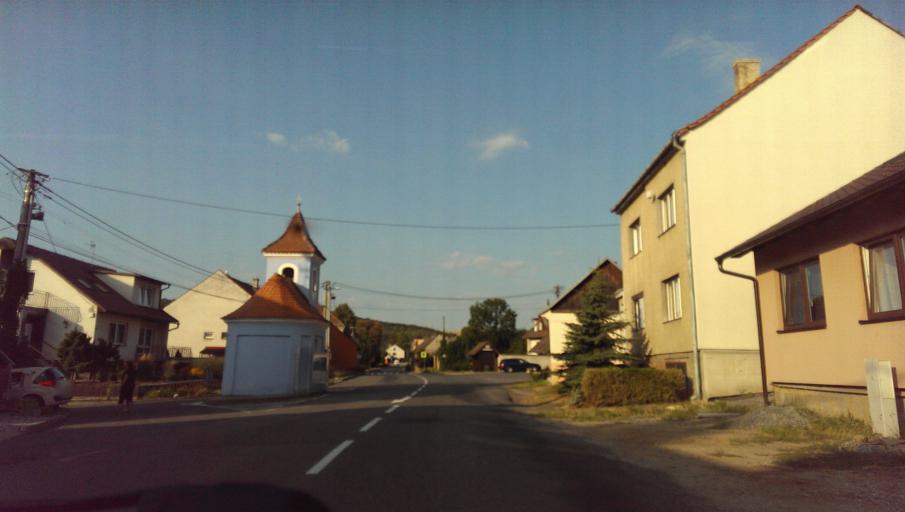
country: CZ
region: Zlin
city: Polesovice
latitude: 49.0569
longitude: 17.3081
